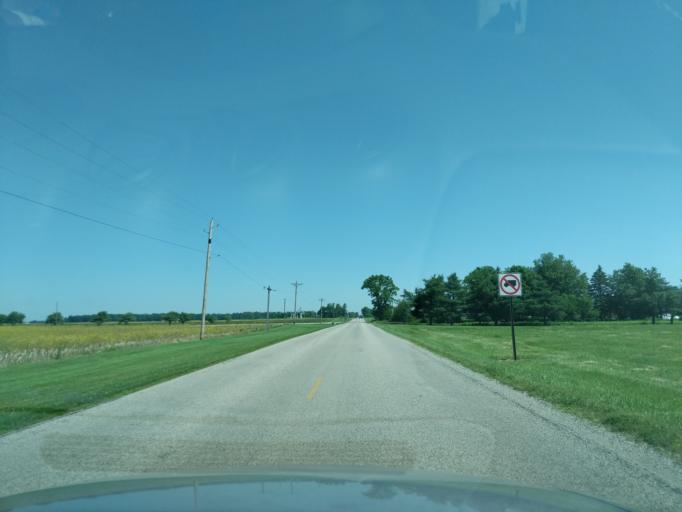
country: US
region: Indiana
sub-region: Huntington County
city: Huntington
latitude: 40.7854
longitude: -85.5077
